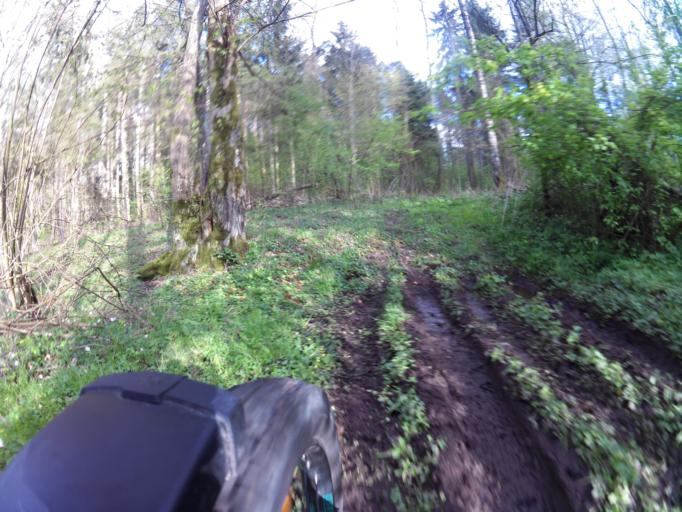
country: PL
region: West Pomeranian Voivodeship
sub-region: Powiat gryficki
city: Ploty
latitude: 53.7841
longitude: 15.2528
